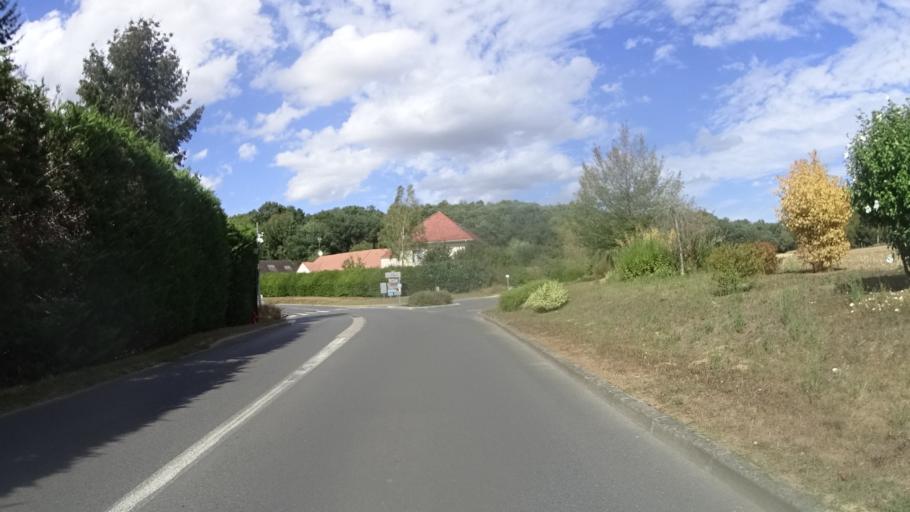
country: FR
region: Ile-de-France
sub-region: Departement de l'Essonne
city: Boutigny-sur-Essonne
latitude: 48.4485
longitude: 2.3671
